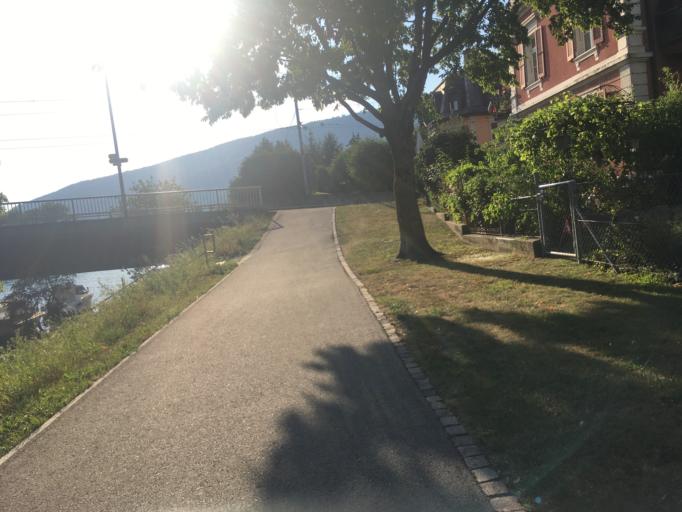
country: CH
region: Bern
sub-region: Biel/Bienne District
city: Nidau
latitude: 47.1221
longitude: 7.2424
